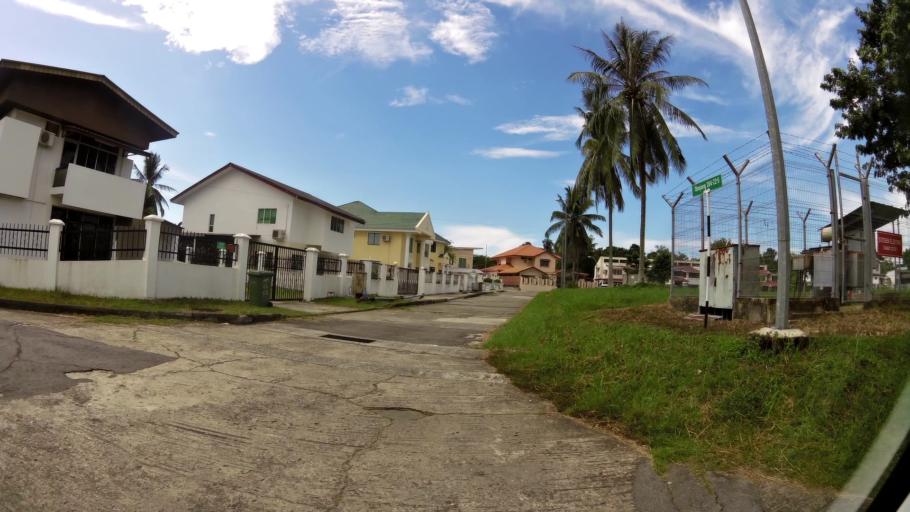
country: BN
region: Brunei and Muara
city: Bandar Seri Begawan
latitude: 4.9675
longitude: 114.9487
